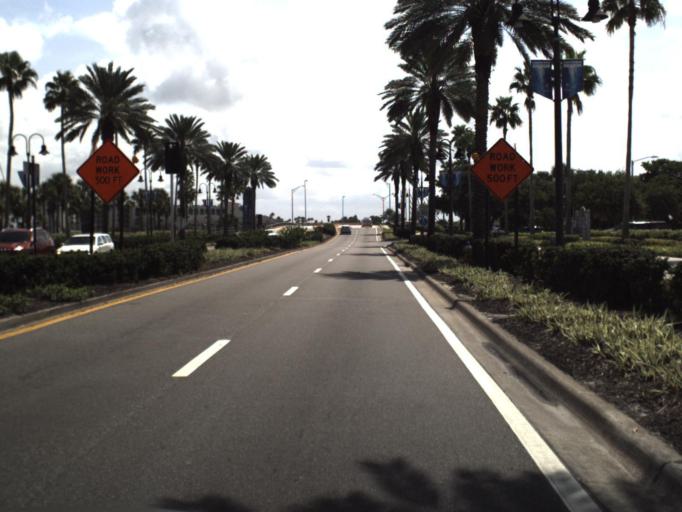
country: US
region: Florida
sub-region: Pinellas County
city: Clearwater
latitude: 27.9775
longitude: -82.8263
